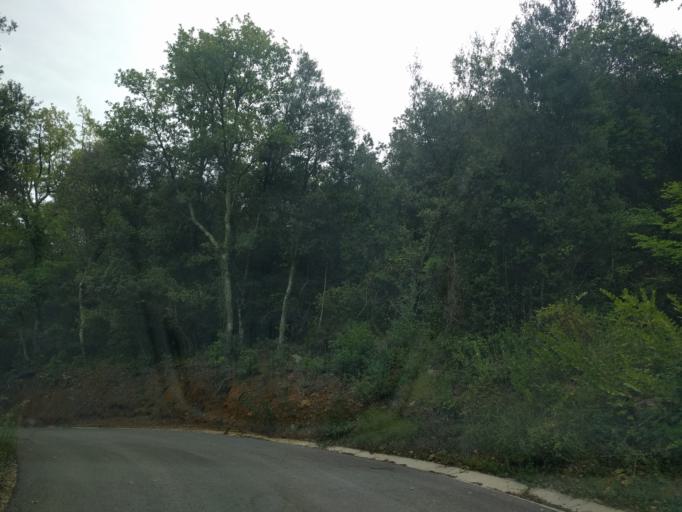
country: ES
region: Catalonia
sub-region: Provincia de Girona
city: la Cellera de Ter
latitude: 42.0289
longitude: 2.6241
